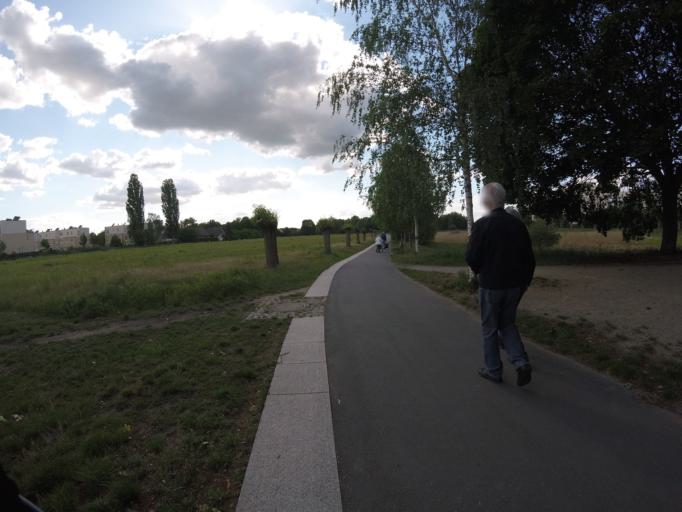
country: DE
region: Berlin
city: Staaken
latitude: 52.5290
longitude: 13.1486
